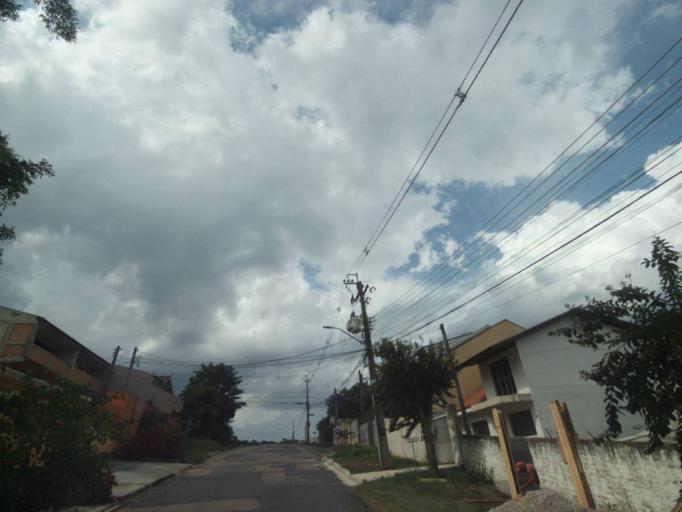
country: BR
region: Parana
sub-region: Curitiba
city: Curitiba
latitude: -25.4558
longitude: -49.3453
